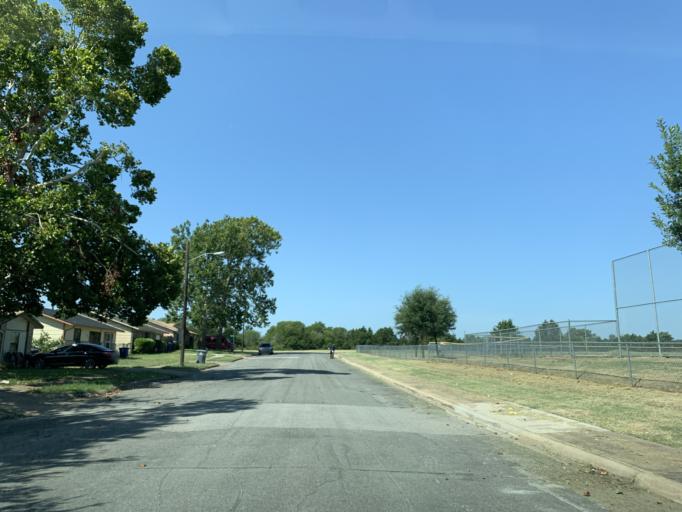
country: US
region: Texas
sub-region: Dallas County
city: Hutchins
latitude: 32.6603
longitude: -96.7583
